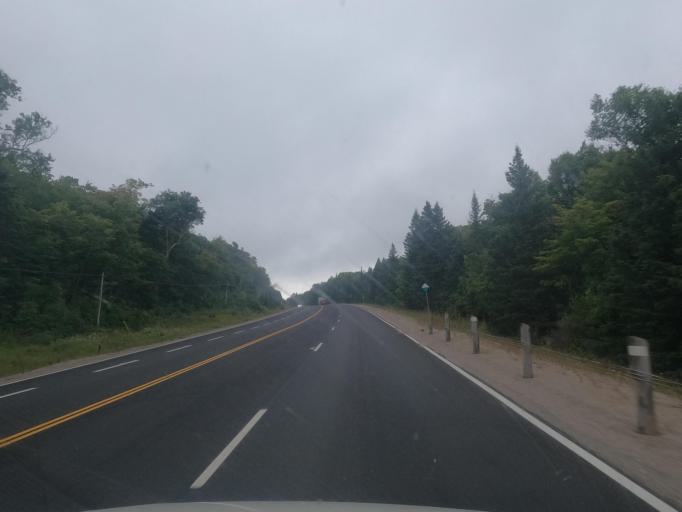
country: CA
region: Ontario
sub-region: Algoma
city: Sault Ste. Marie
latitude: 47.1911
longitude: -84.6688
